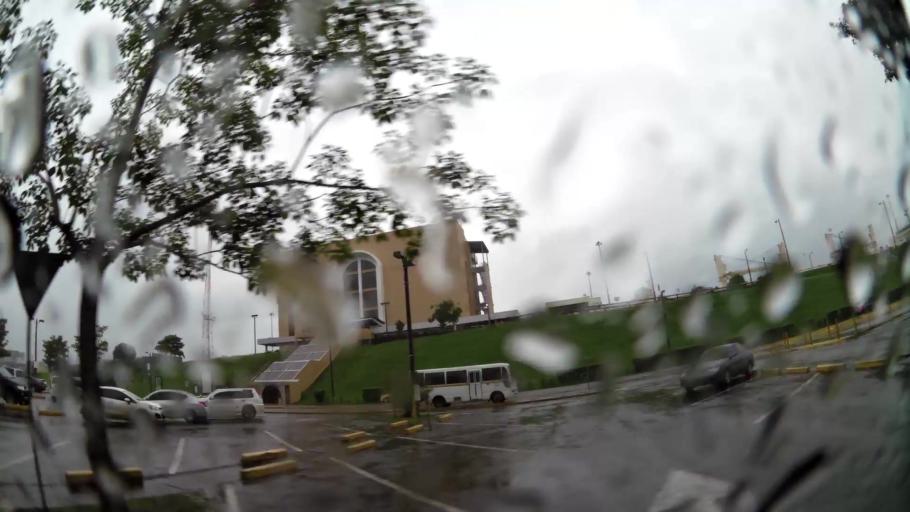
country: PA
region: Panama
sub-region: Distrito de Panama
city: Paraiso
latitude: 8.9982
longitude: -79.5907
